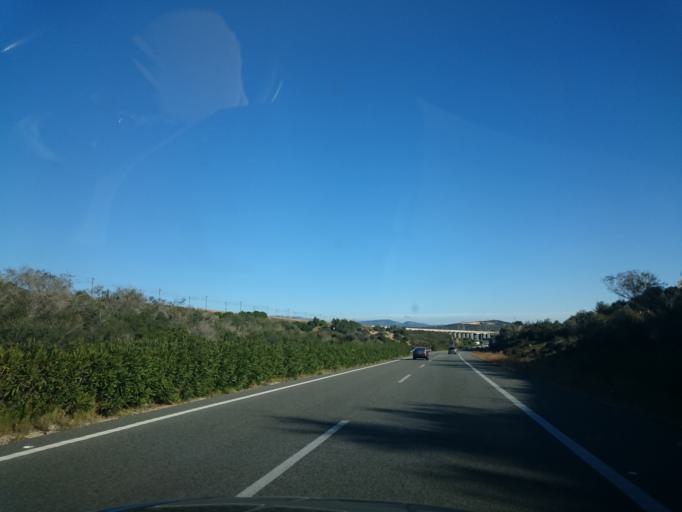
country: ES
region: Catalonia
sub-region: Provincia de Tarragona
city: Amposta
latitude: 40.7200
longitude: 0.5628
